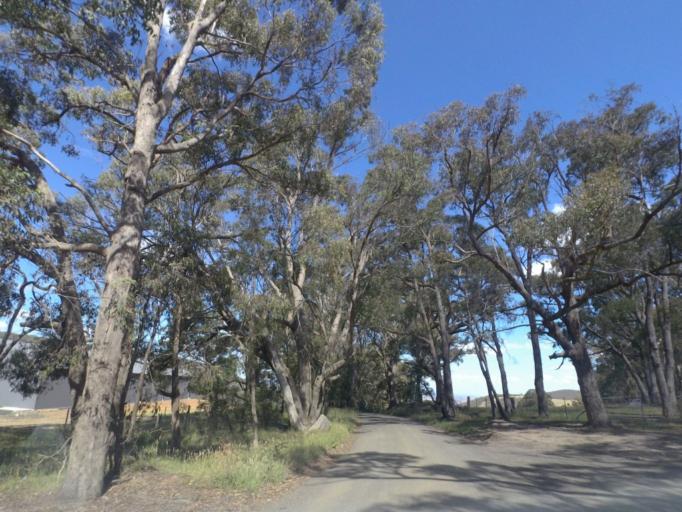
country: AU
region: Victoria
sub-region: Hume
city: Sunbury
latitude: -37.4247
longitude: 144.6400
